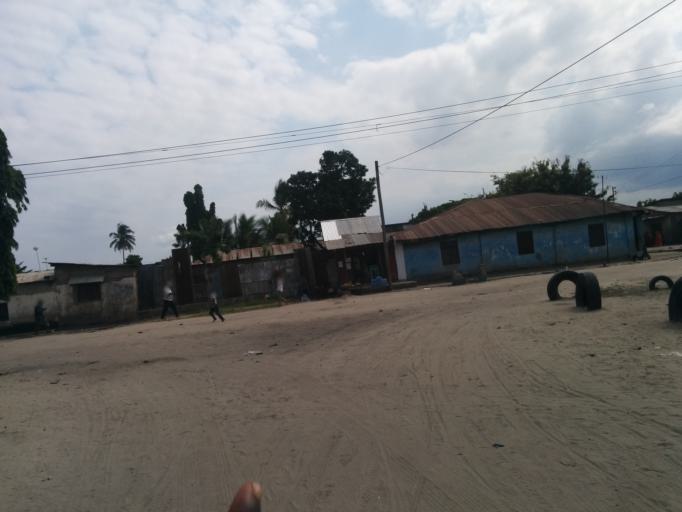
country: TZ
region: Dar es Salaam
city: Dar es Salaam
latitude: -6.8670
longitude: 39.2545
